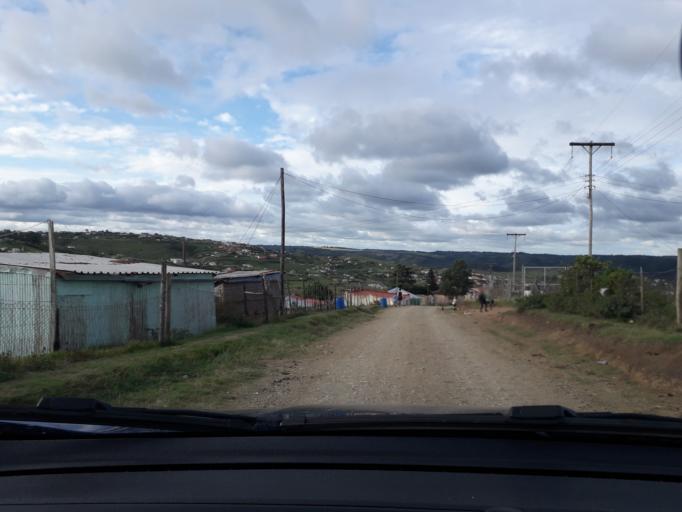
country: ZA
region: Eastern Cape
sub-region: Buffalo City Metropolitan Municipality
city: East London
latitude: -32.8053
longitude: 27.9598
